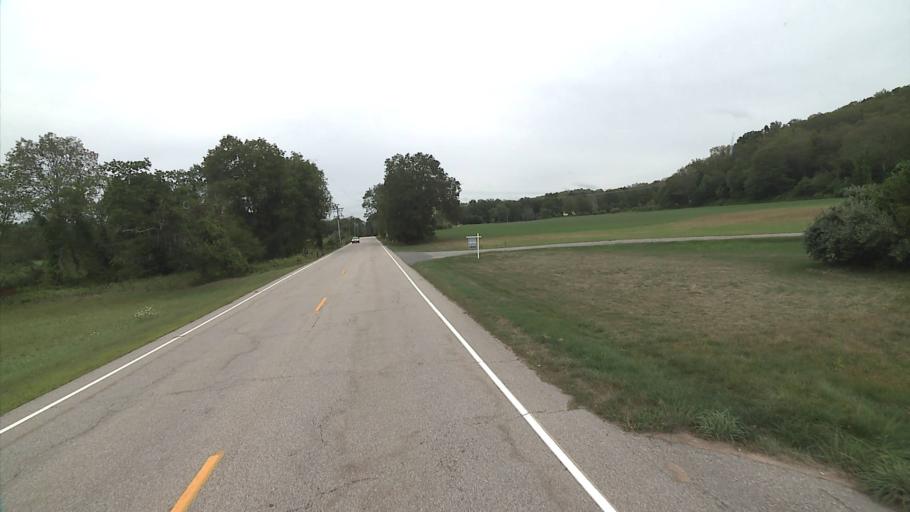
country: US
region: Connecticut
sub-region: Middlesex County
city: Essex Village
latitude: 41.4227
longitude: -72.3346
